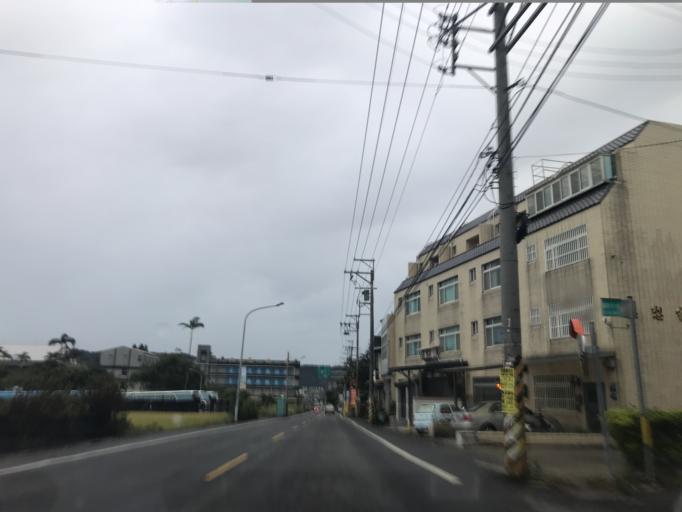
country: TW
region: Taiwan
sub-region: Hsinchu
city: Zhubei
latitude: 24.8305
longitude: 121.0845
